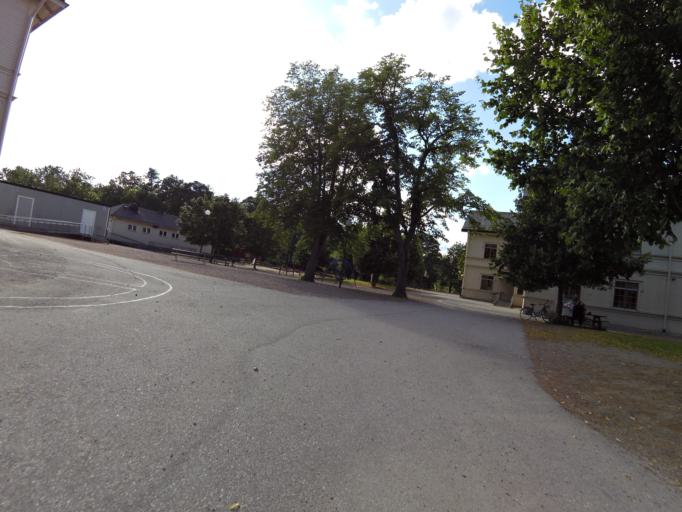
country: SE
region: Gaevleborg
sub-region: Gavle Kommun
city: Gavle
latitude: 60.7043
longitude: 17.1587
